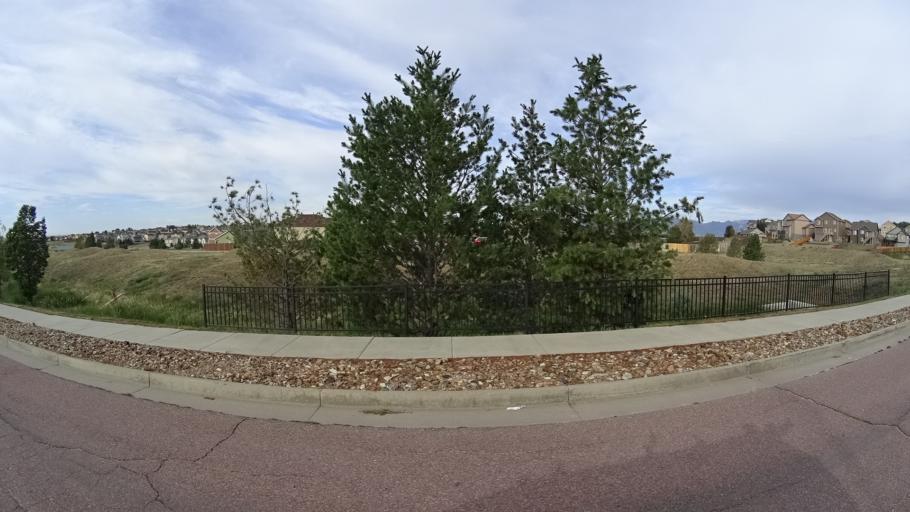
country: US
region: Colorado
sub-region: El Paso County
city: Fountain
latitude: 38.7168
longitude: -104.6868
